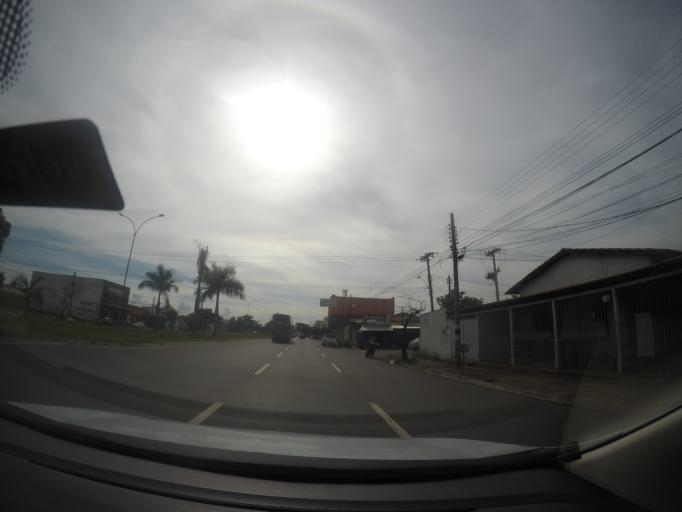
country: BR
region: Goias
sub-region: Goiania
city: Goiania
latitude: -16.6645
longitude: -49.2764
